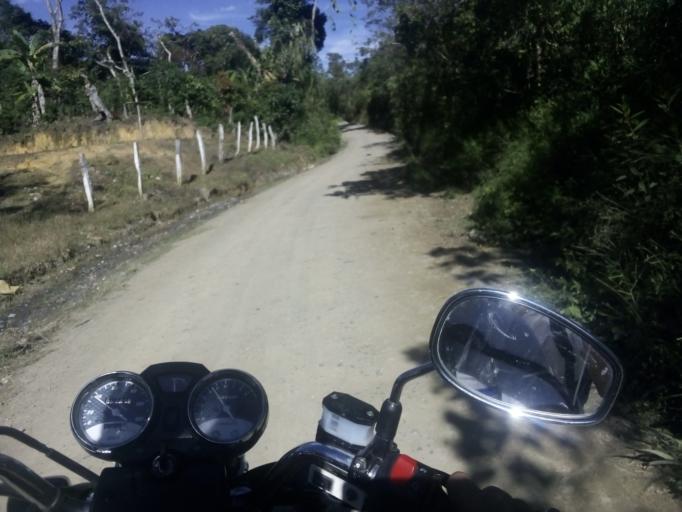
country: CO
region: Santander
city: Guepsa
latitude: 6.0064
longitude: -73.5508
